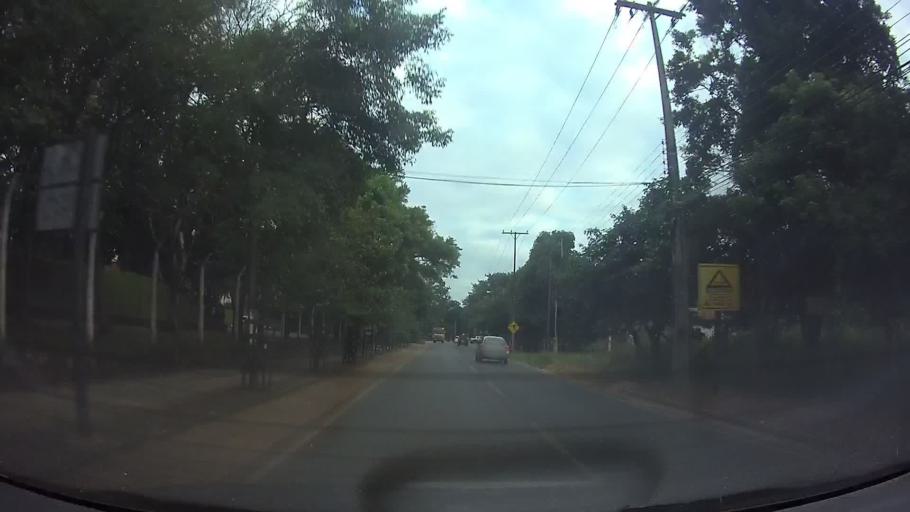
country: PY
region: Central
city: San Lorenzo
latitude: -25.3015
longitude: -57.4911
